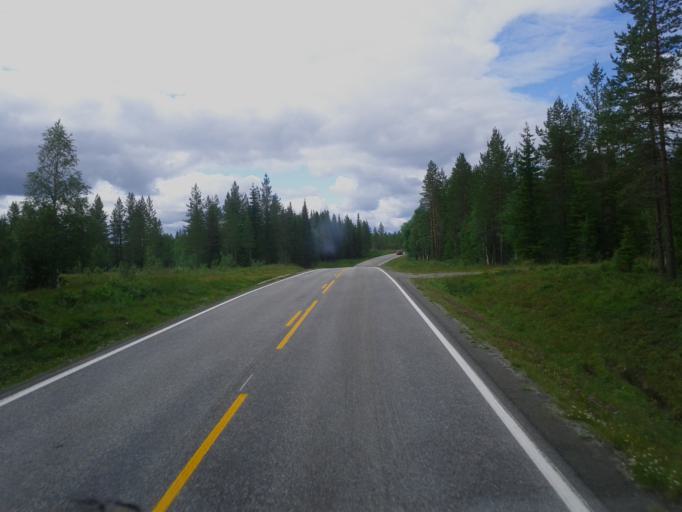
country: NO
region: Nord-Trondelag
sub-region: Hoylandet
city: Hoylandet
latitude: 64.6504
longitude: 12.6432
